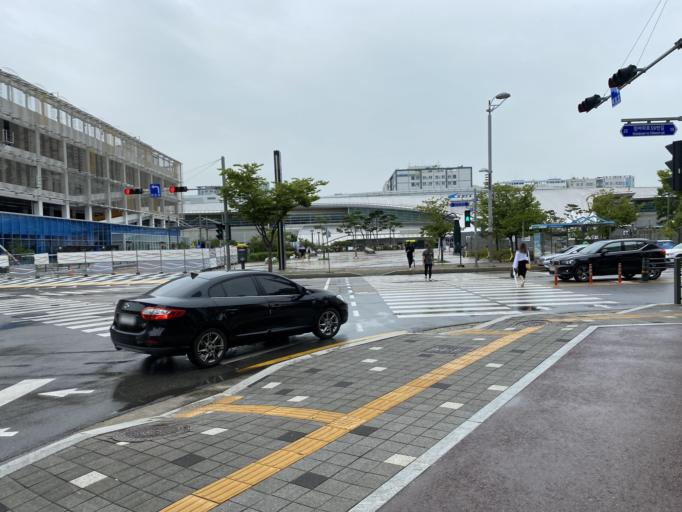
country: KR
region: Incheon
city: Incheon
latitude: 37.4939
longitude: 126.4924
